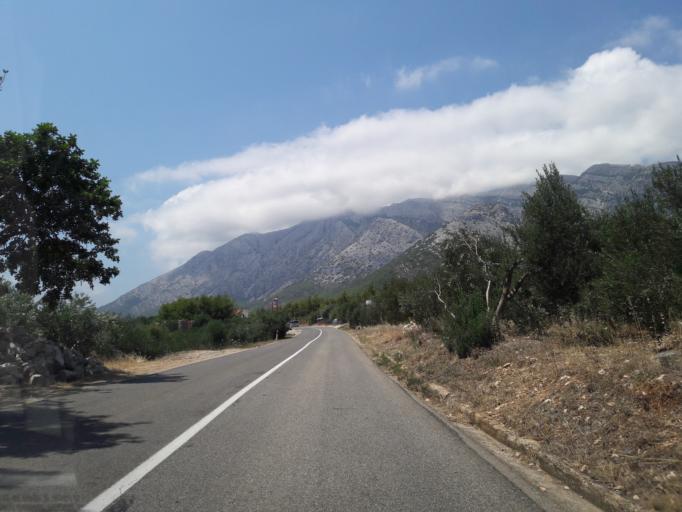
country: HR
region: Dubrovacko-Neretvanska
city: Orebic
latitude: 42.9835
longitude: 17.2042
